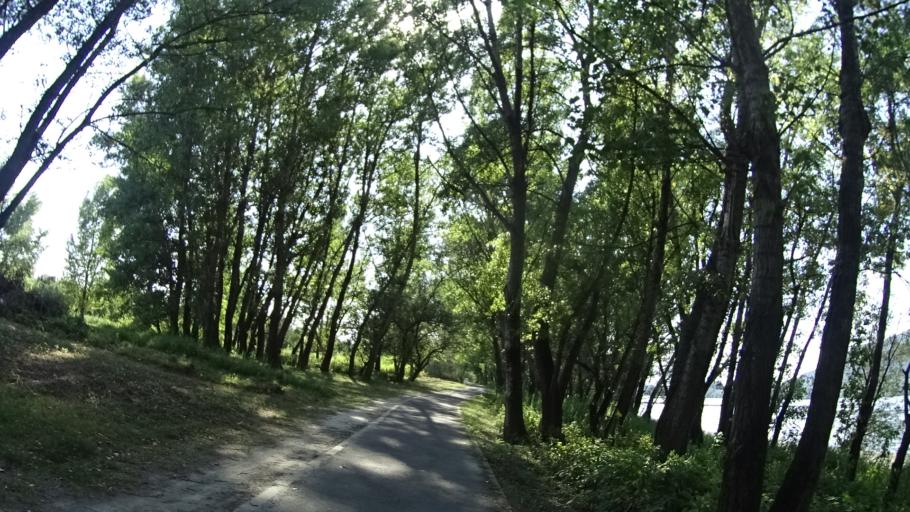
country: HU
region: Komarom-Esztergom
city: Esztergom
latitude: 47.8163
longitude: 18.7761
